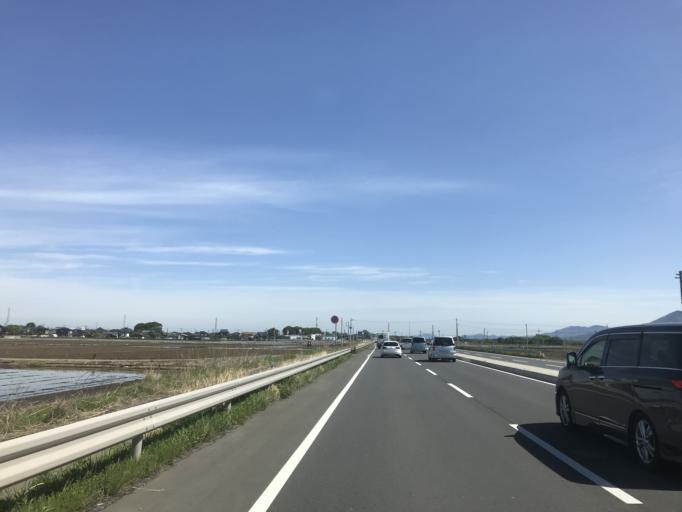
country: JP
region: Ibaraki
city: Ishige
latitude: 36.1547
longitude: 139.9939
